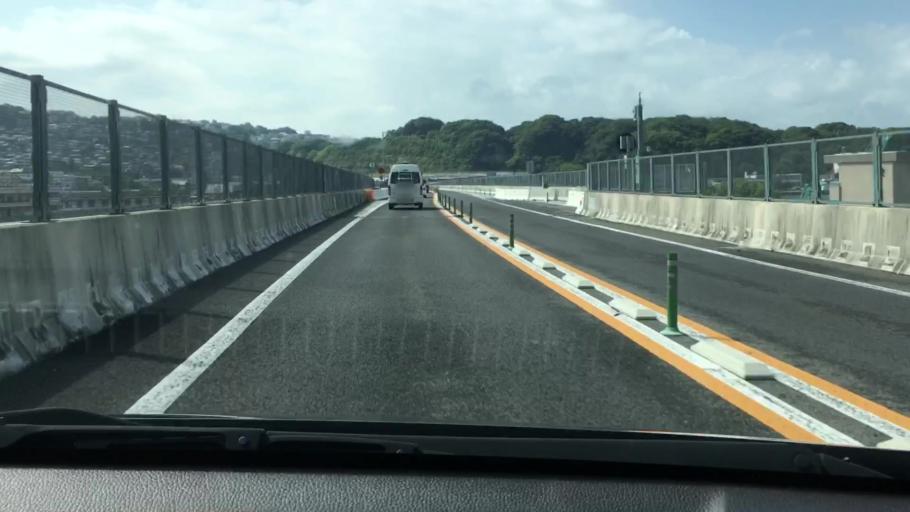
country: JP
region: Nagasaki
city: Sasebo
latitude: 33.1604
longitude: 129.7287
